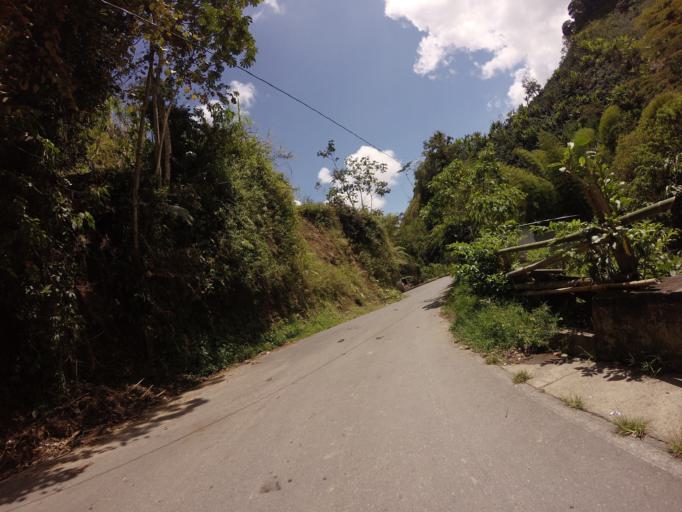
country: CO
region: Caldas
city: Marquetalia
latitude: 5.2925
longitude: -75.1062
